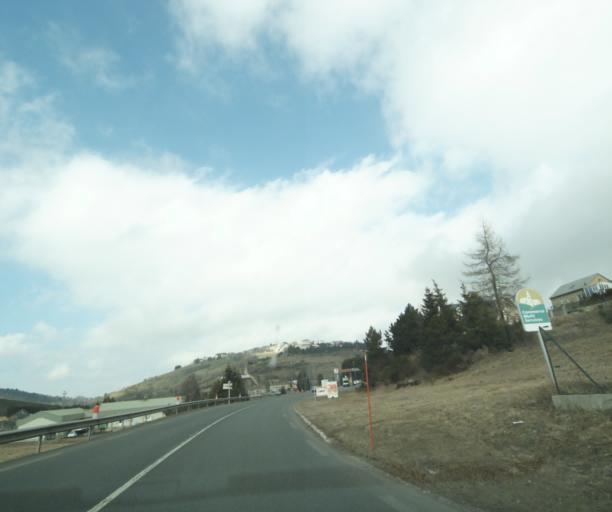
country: FR
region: Languedoc-Roussillon
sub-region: Departement de la Lozere
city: Langogne
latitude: 44.6308
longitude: 3.6757
